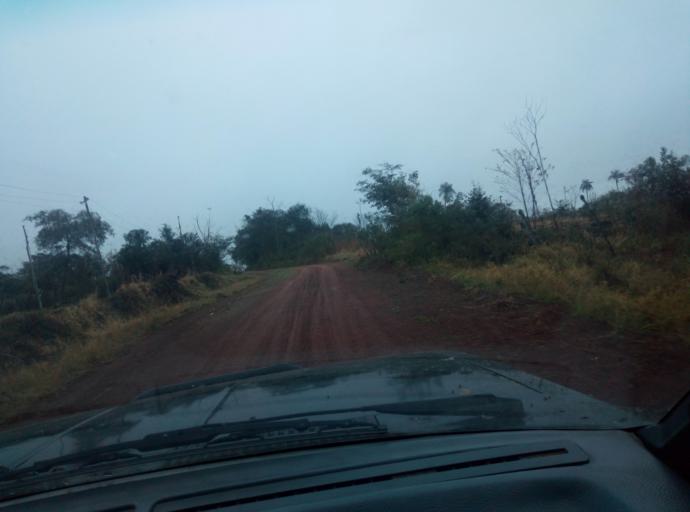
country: PY
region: Caaguazu
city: Carayao
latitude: -25.1904
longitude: -56.3188
